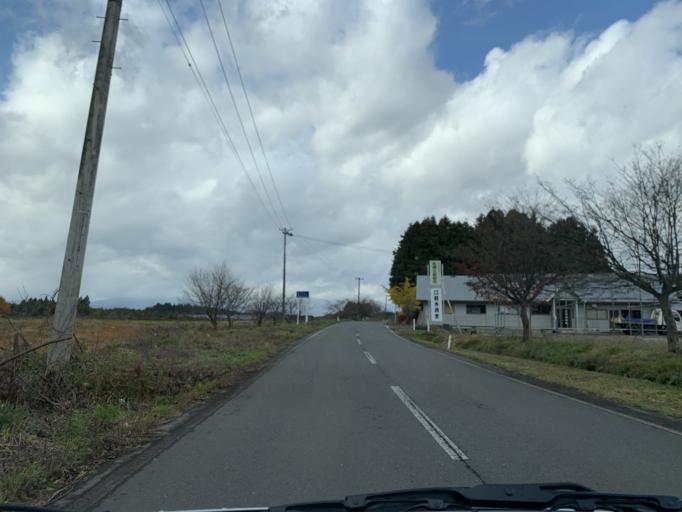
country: JP
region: Iwate
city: Mizusawa
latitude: 39.0664
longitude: 141.0797
